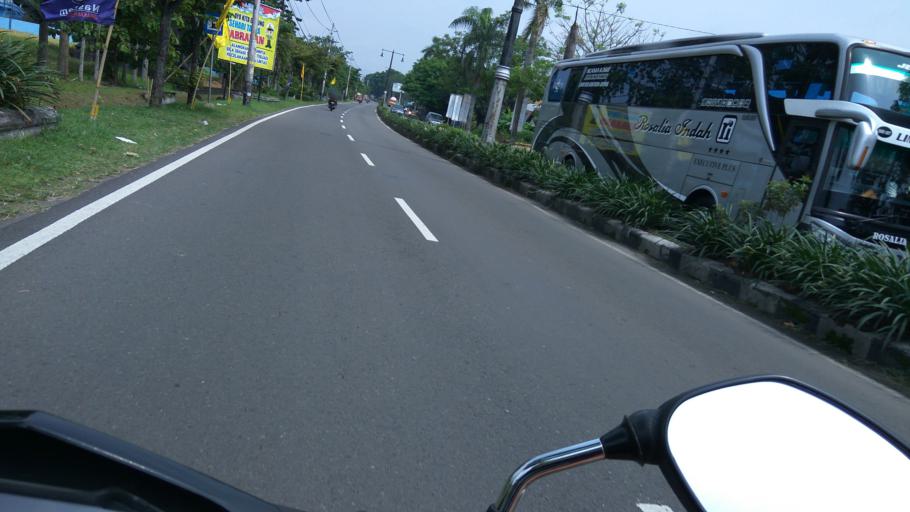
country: ID
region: Central Java
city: Jaten
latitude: -7.5862
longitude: 110.9185
